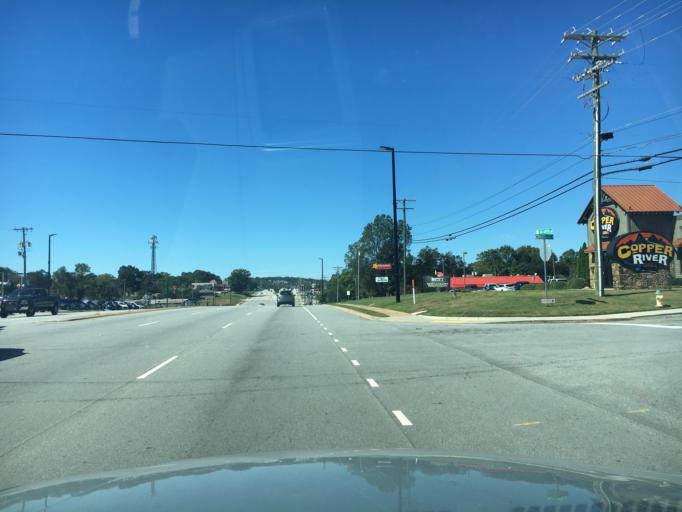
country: US
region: South Carolina
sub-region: Greenville County
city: Greer
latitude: 34.9479
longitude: -82.2172
